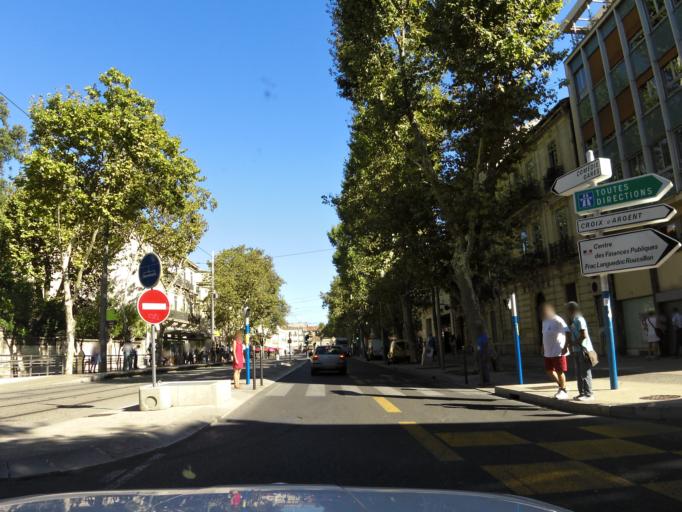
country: FR
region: Languedoc-Roussillon
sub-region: Departement de l'Herault
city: Montpellier
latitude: 43.6065
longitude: 3.8721
